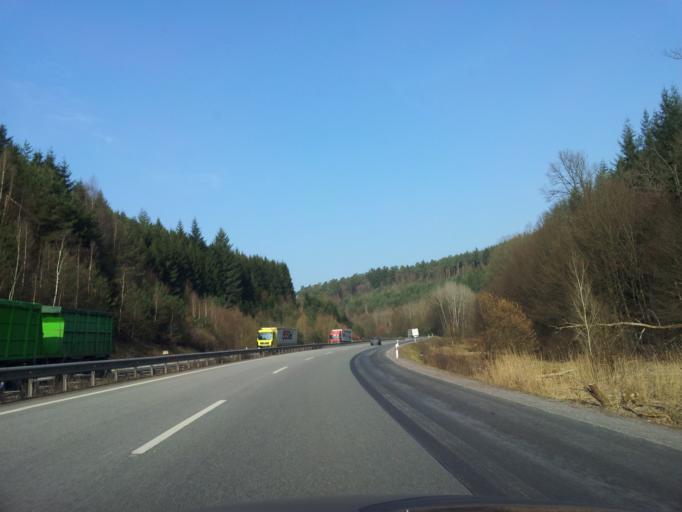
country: DE
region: Rheinland-Pfalz
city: Ruppertsweiler
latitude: 49.2112
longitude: 7.6650
